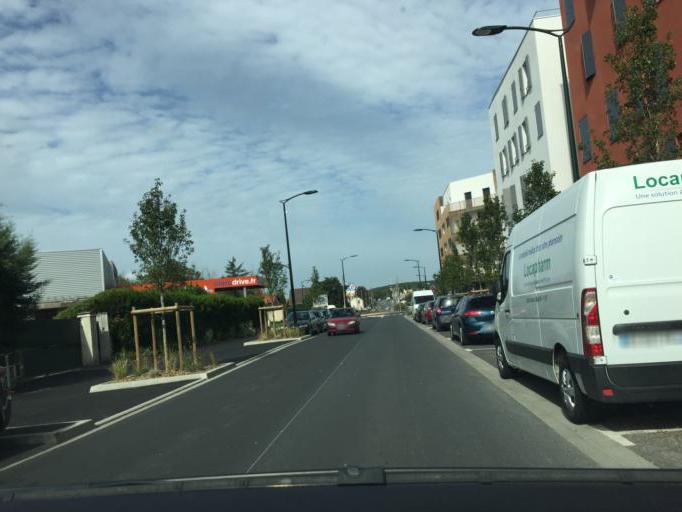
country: FR
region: Ile-de-France
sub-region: Departement de l'Essonne
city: Palaiseau
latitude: 48.7252
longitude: 2.2467
